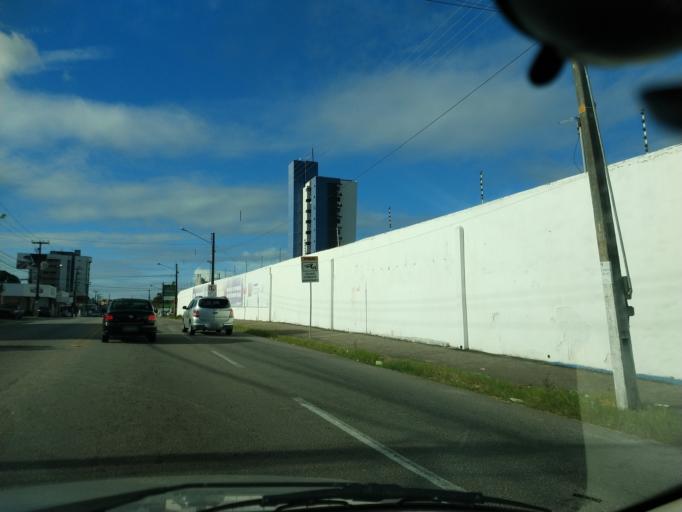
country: BR
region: Rio Grande do Norte
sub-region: Natal
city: Natal
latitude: -5.8140
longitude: -35.2166
